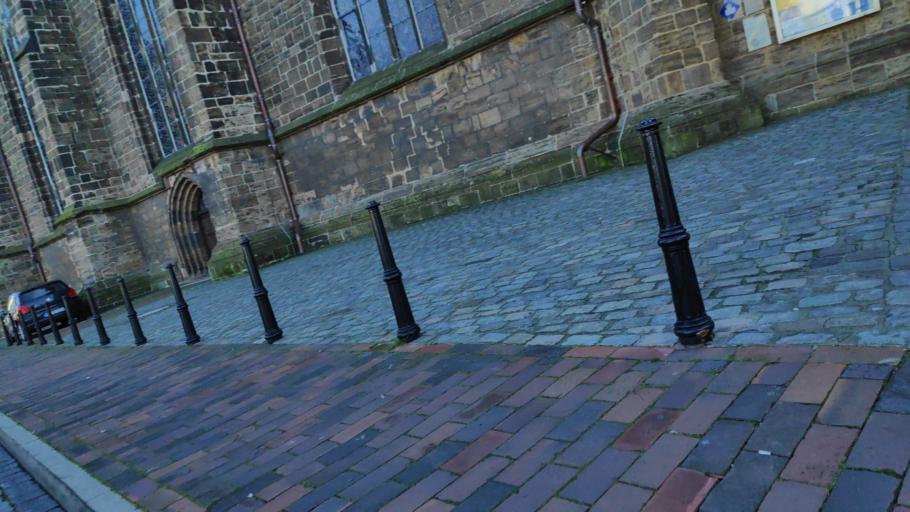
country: DE
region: North Rhine-Westphalia
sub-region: Regierungsbezirk Detmold
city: Minden
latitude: 52.2883
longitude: 8.9149
